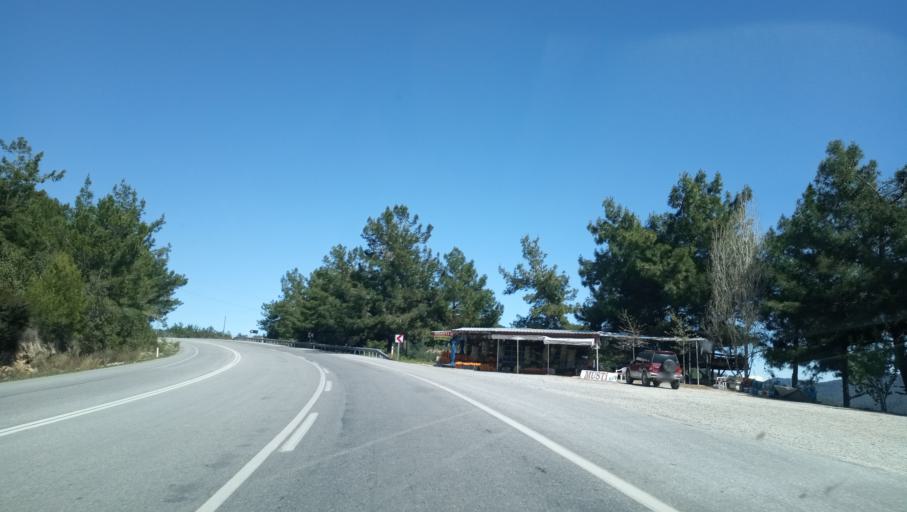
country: TR
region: Antalya
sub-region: Manavgat
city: Kizilagac
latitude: 36.7597
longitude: 31.6395
